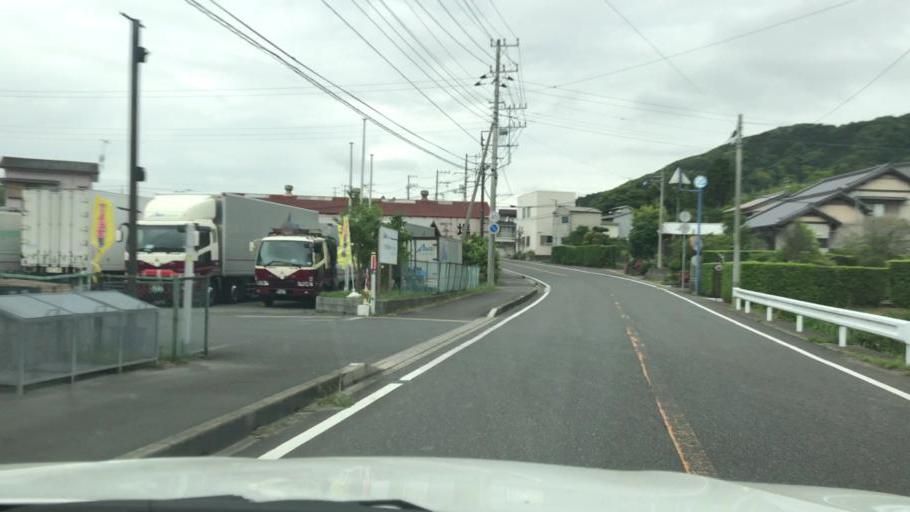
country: JP
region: Chiba
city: Kawaguchi
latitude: 35.1229
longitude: 140.0954
